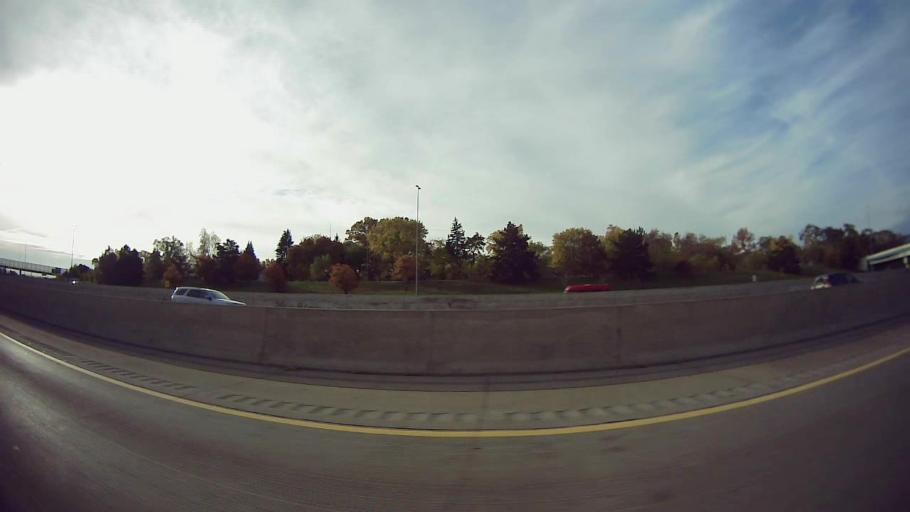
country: US
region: Michigan
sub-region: Wayne County
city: Redford
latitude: 42.3856
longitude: -83.2437
